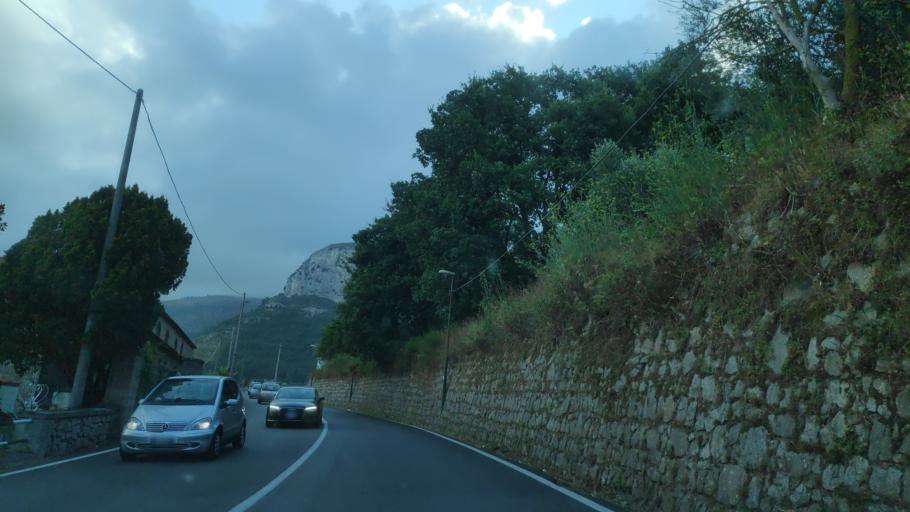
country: IT
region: Campania
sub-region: Provincia di Napoli
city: Piano di Sorrento
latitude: 40.6206
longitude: 14.4196
